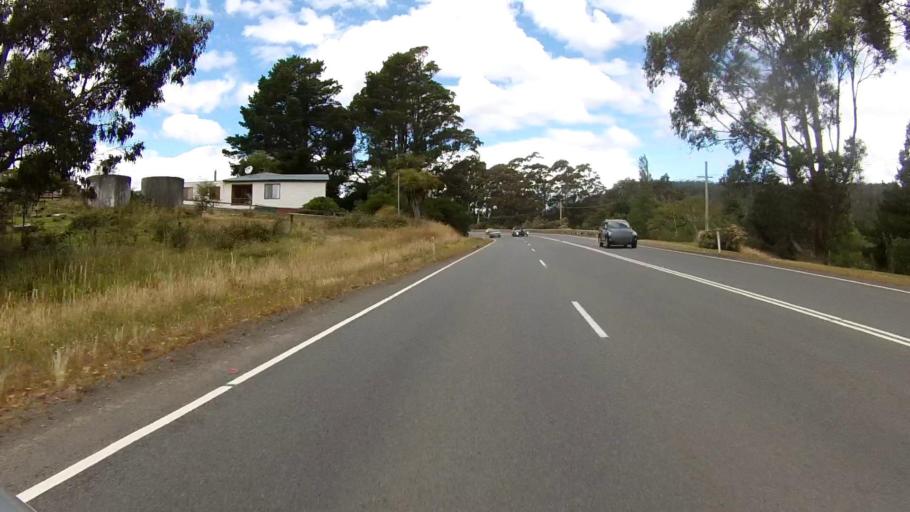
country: AU
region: Tasmania
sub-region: Huon Valley
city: Huonville
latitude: -42.9764
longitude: 147.1509
